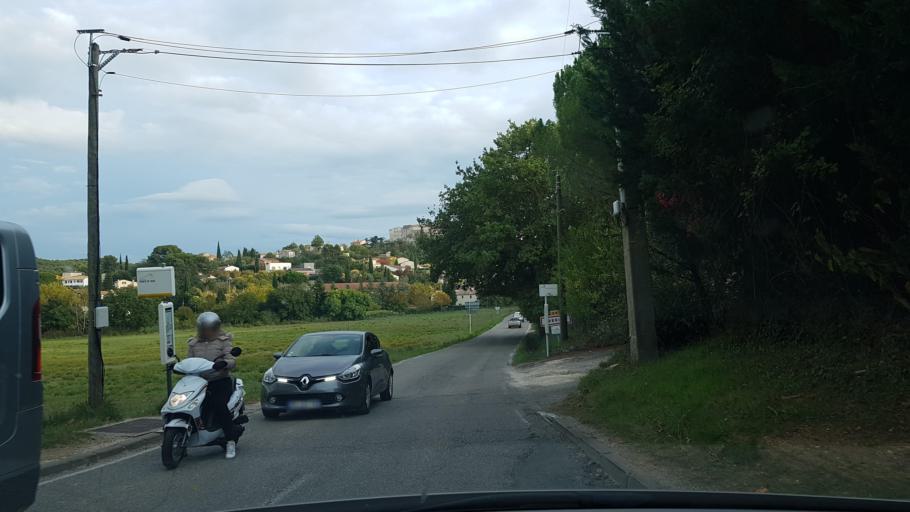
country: FR
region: Provence-Alpes-Cote d'Azur
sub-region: Departement des Bouches-du-Rhone
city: Cabries
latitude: 43.4448
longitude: 5.3725
